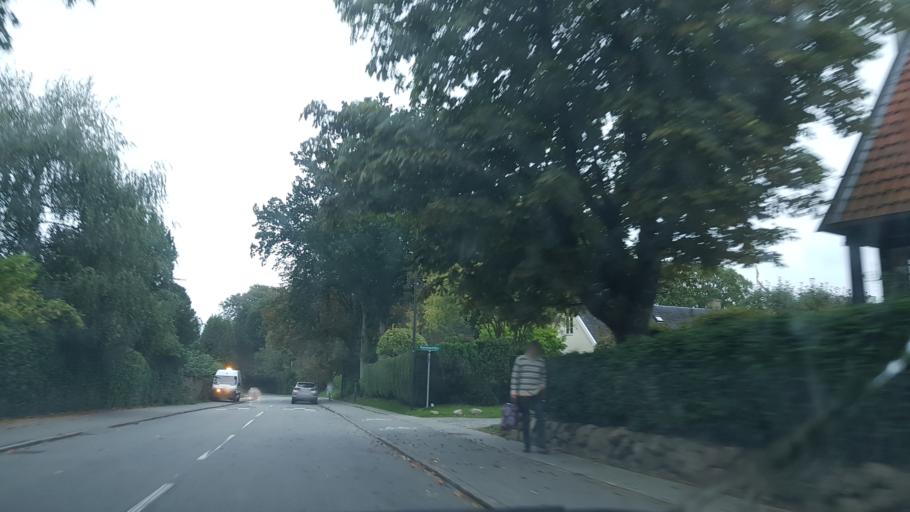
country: DK
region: Capital Region
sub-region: Rudersdal Kommune
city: Trorod
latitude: 55.8396
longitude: 12.5485
